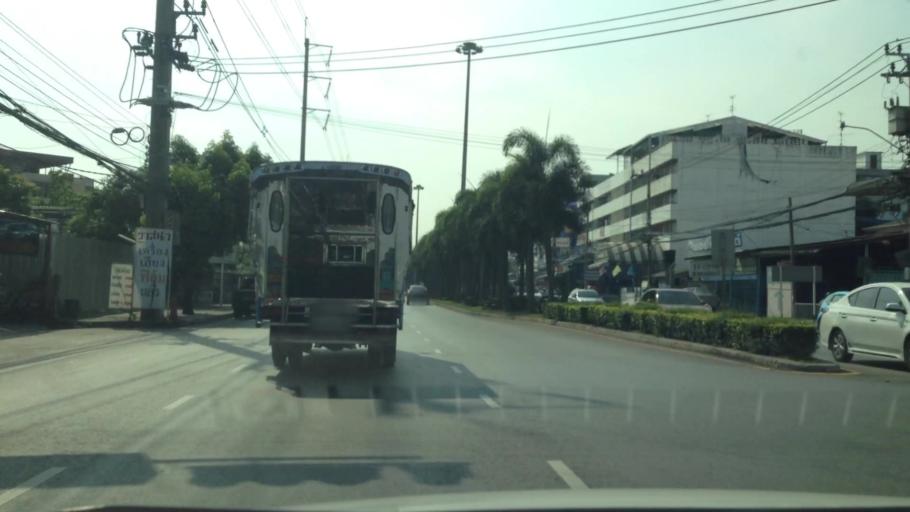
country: TH
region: Samut Prakan
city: Samut Prakan
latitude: 13.5839
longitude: 100.6004
